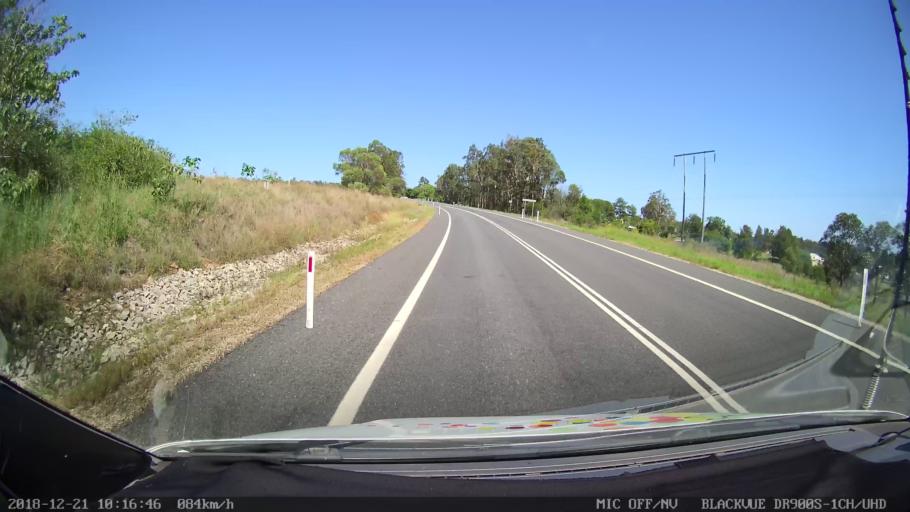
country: AU
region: New South Wales
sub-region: Clarence Valley
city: South Grafton
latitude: -29.6828
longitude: 152.8801
